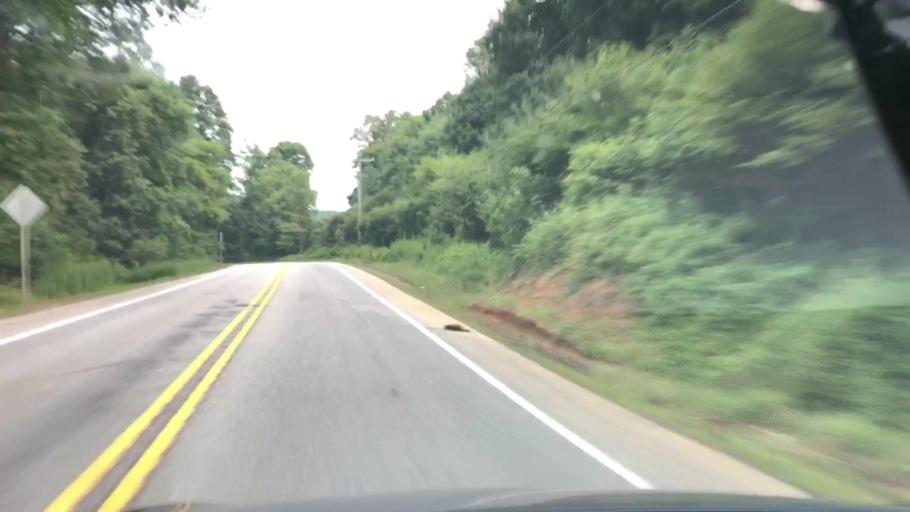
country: US
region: Pennsylvania
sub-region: Venango County
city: Hasson Heights
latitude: 41.5143
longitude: -79.7046
